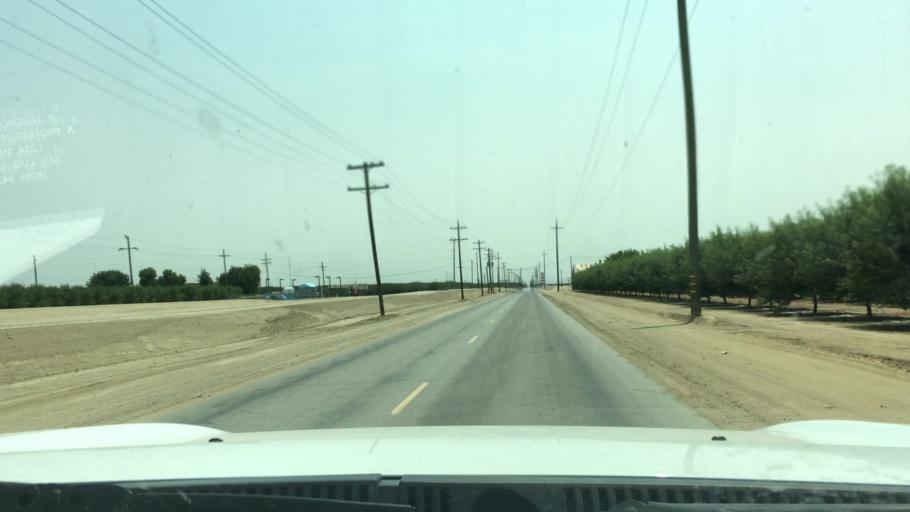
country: US
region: California
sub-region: Kern County
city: Wasco
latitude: 35.6114
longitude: -119.4380
